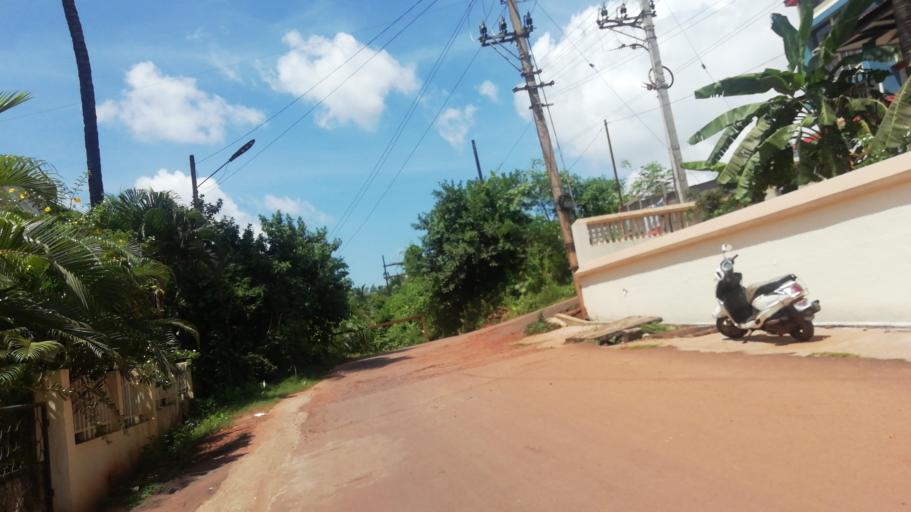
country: IN
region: Goa
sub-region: North Goa
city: Queula
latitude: 15.3943
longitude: 73.9974
